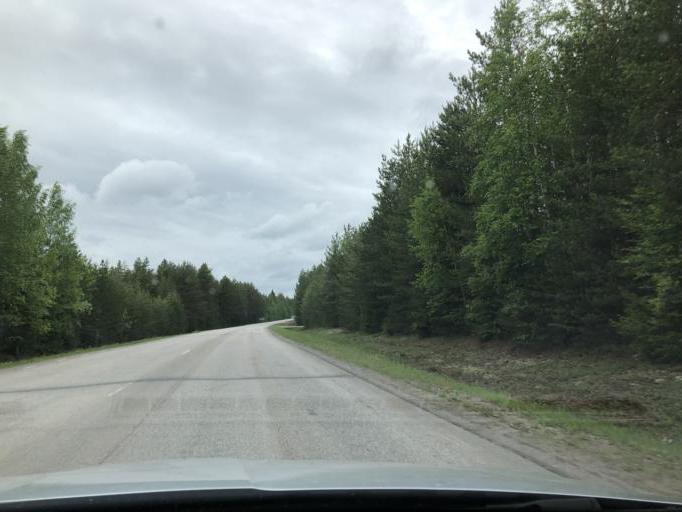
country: SE
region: Norrbotten
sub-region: Pitea Kommun
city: Bergsviken
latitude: 65.3664
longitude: 21.3623
